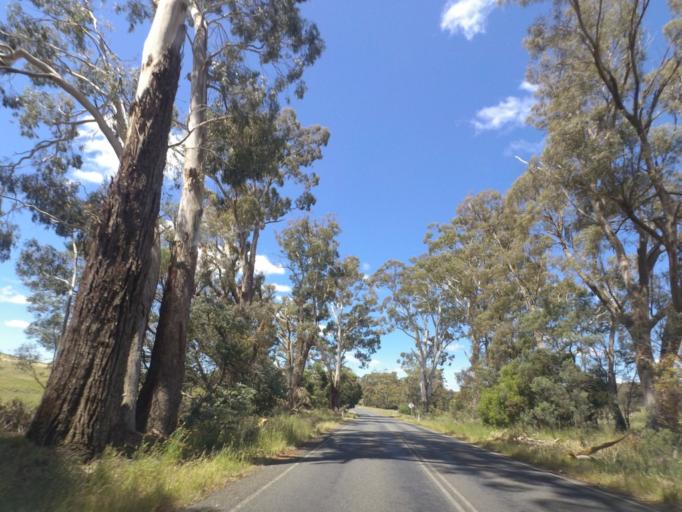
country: AU
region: Victoria
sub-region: Mount Alexander
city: Castlemaine
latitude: -37.3153
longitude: 144.2229
